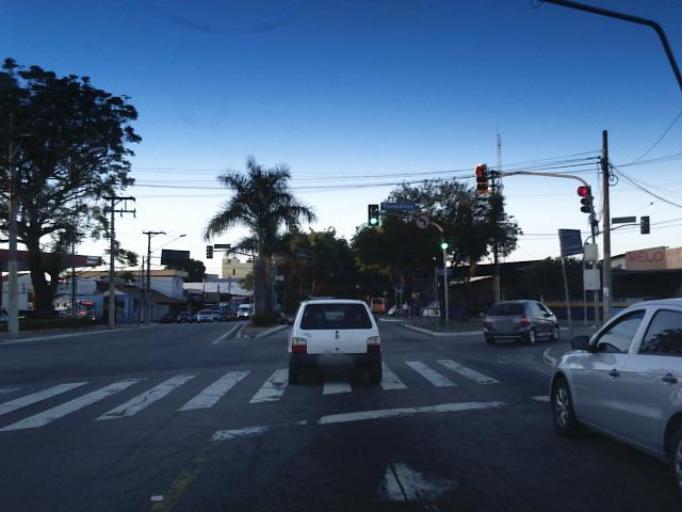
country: BR
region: Sao Paulo
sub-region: Sao Jose Dos Campos
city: Sao Jose dos Campos
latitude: -23.1932
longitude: -45.8756
